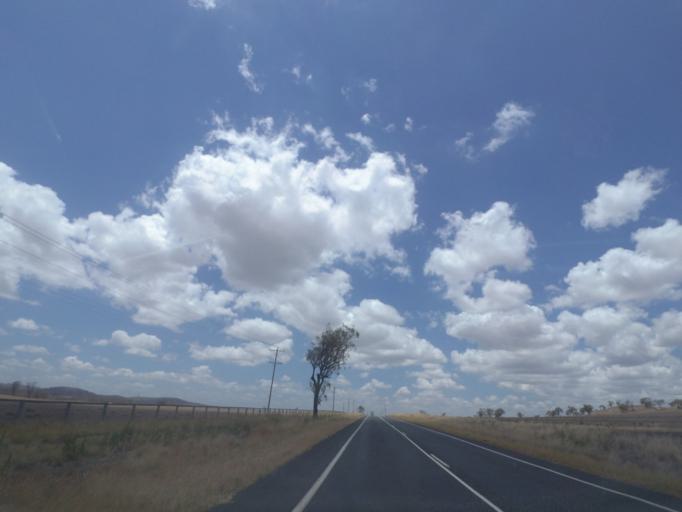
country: AU
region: Queensland
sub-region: Toowoomba
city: Top Camp
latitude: -27.7458
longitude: 151.9281
